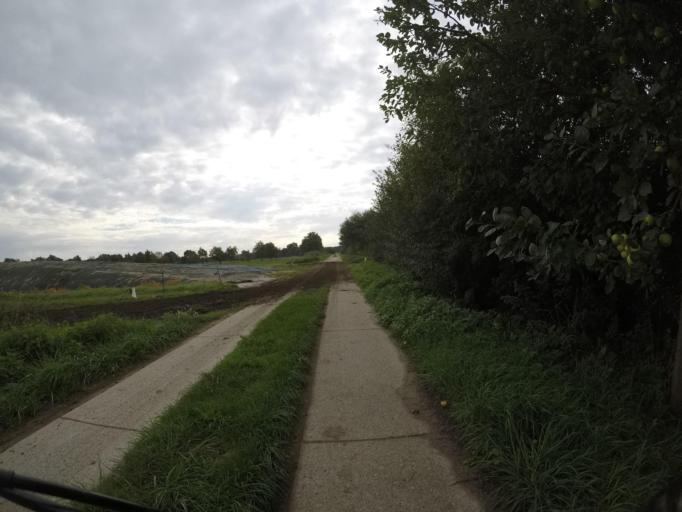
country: DE
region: Lower Saxony
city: Neu Darchau
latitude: 53.2851
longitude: 10.8727
